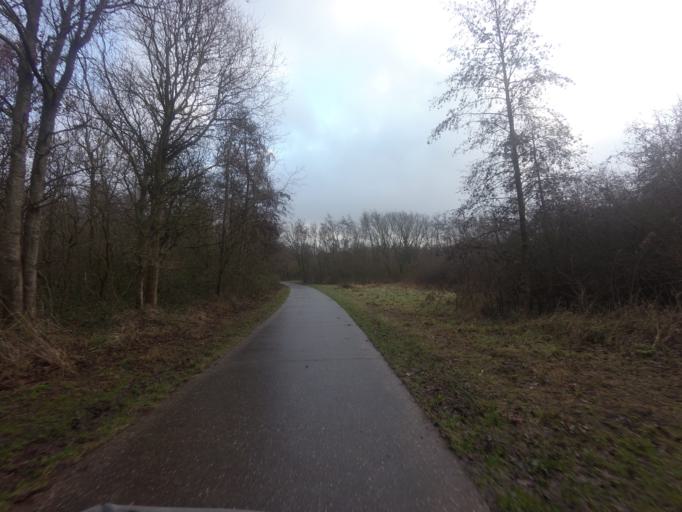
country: NL
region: North Holland
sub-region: Gemeente Texel
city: Den Burg
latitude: 53.1657
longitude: 4.8474
